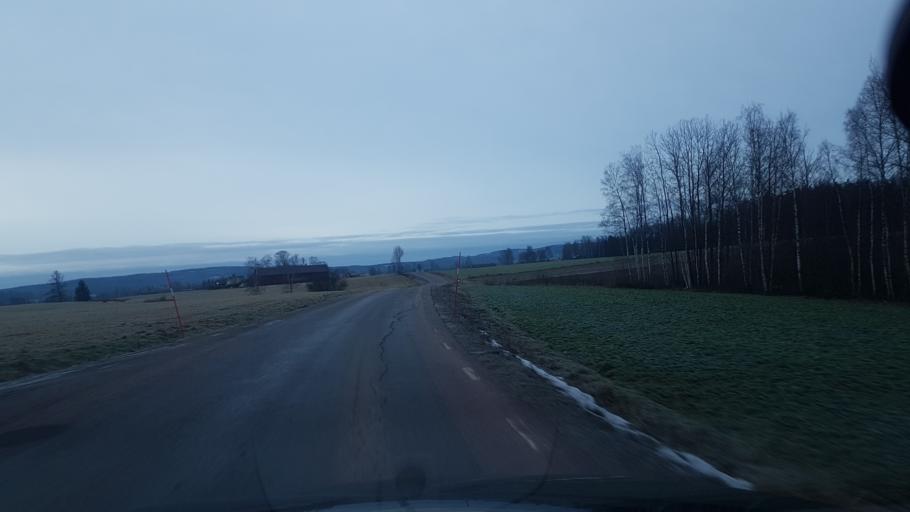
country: SE
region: Dalarna
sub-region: Saters Kommun
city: Saeter
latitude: 60.4340
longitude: 15.6566
